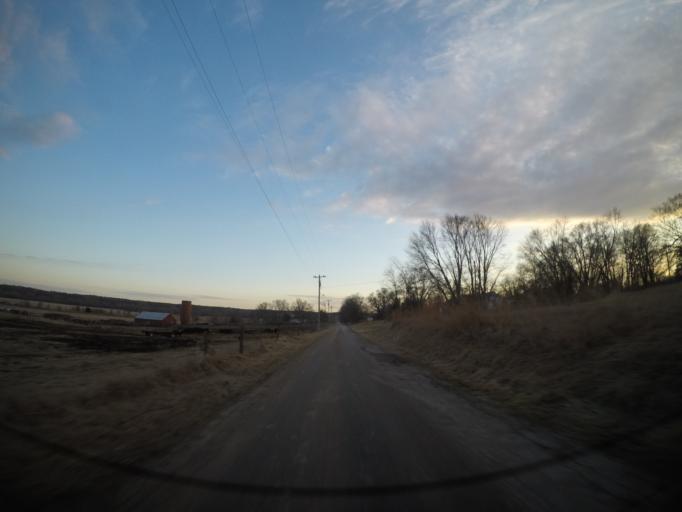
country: US
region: Kansas
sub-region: Wyandotte County
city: Bonner Springs
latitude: 39.0192
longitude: -94.9088
